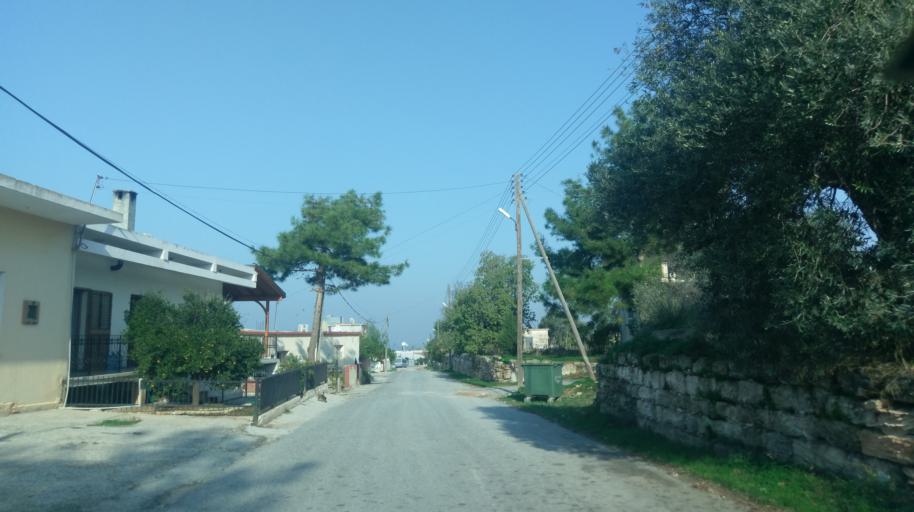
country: CY
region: Ammochostos
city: Leonarisso
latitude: 35.5402
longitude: 34.2169
